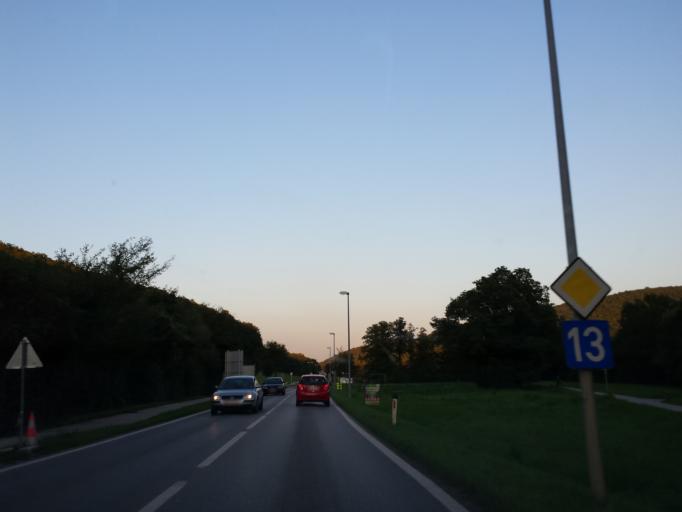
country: AT
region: Lower Austria
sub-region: Politischer Bezirk Modling
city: Kaltenleutgeben
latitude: 48.1382
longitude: 16.2061
